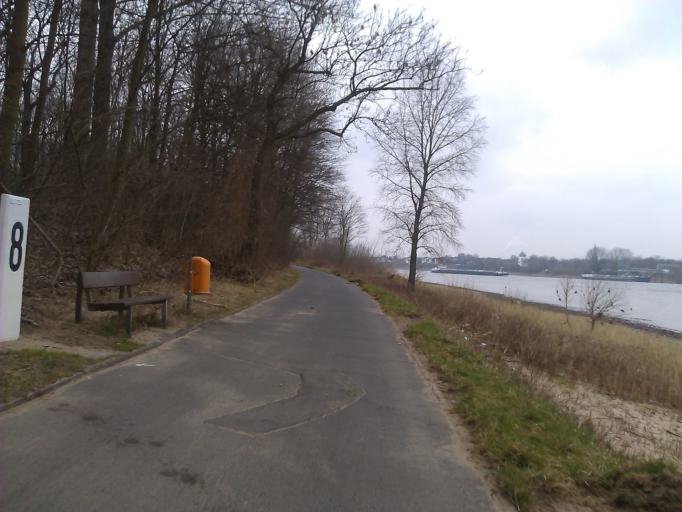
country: DE
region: North Rhine-Westphalia
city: Niederkassel
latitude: 50.8191
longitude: 7.0202
